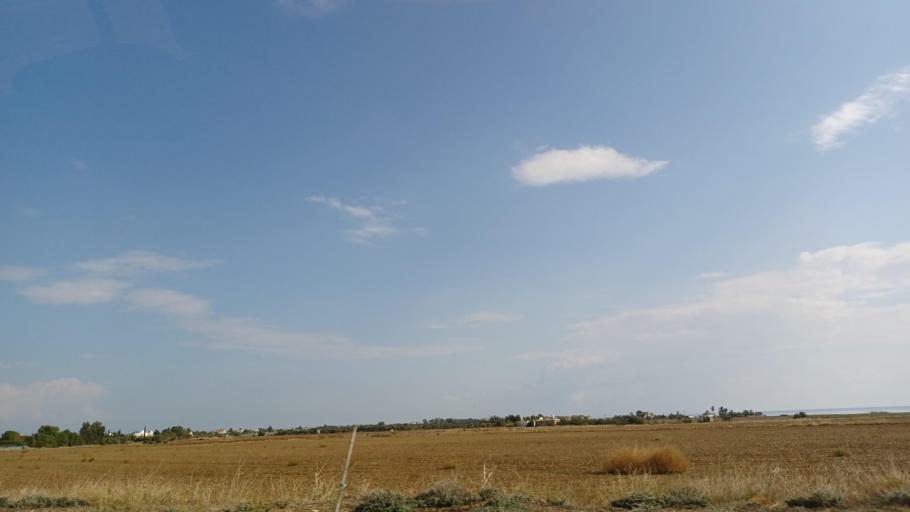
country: CY
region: Larnaka
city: Tersefanou
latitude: 34.8231
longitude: 33.5456
